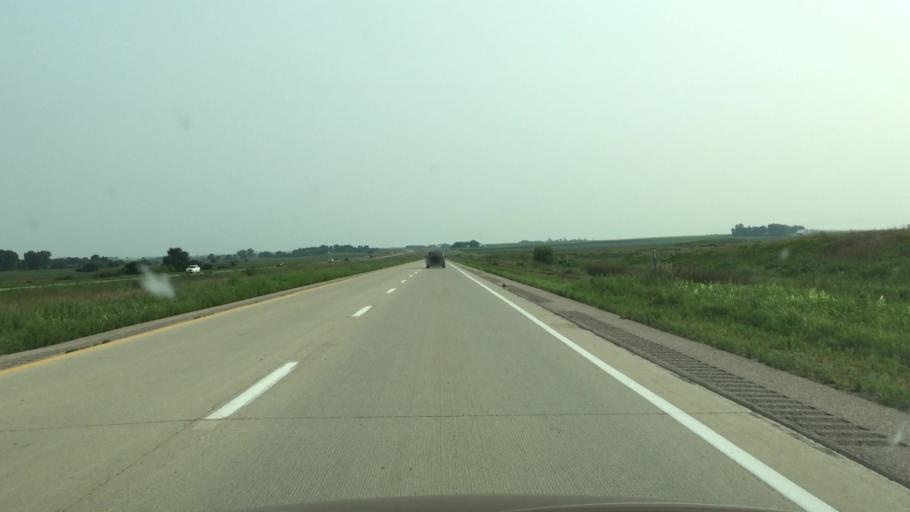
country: US
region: Iowa
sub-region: O'Brien County
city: Sheldon
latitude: 43.1164
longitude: -95.8928
